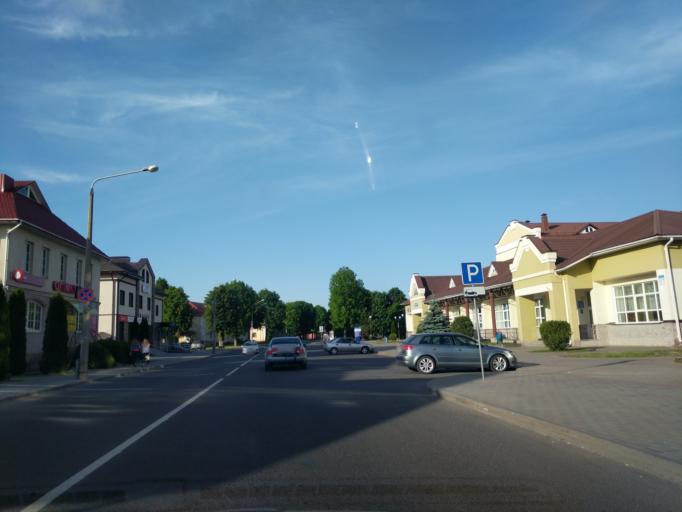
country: BY
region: Grodnenskaya
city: Ashmyany
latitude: 54.4258
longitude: 25.9377
